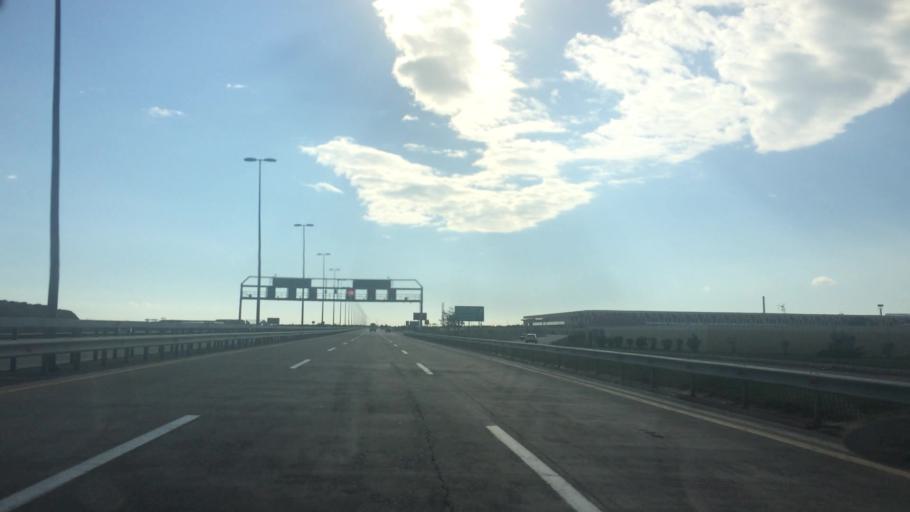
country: AZ
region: Baki
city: Hovsan
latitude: 40.3882
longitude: 50.0684
